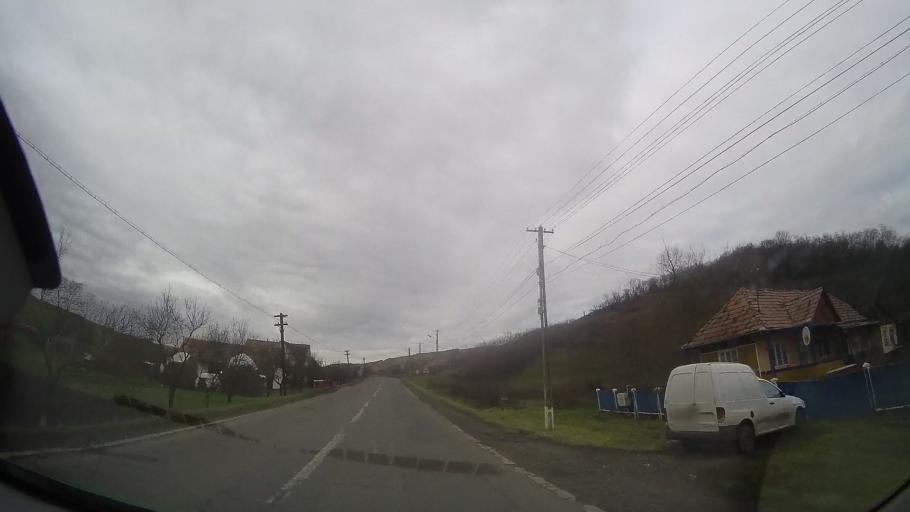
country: RO
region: Mures
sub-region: Comuna Craesti
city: Craiesti
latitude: 46.7587
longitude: 24.4072
